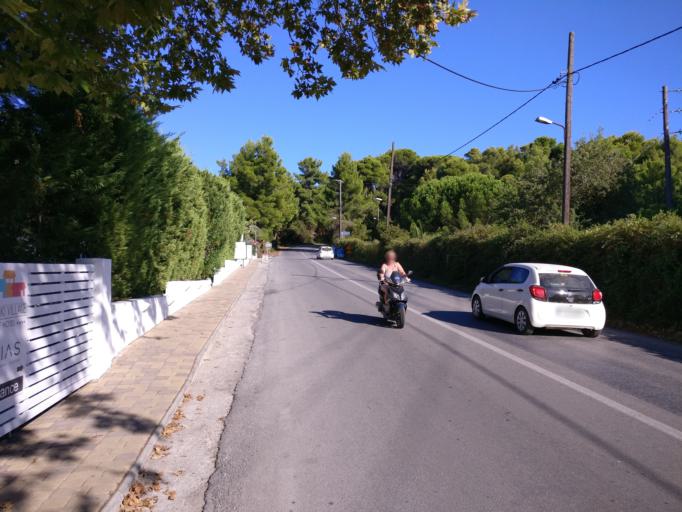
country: GR
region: Thessaly
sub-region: Nomos Magnisias
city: Skiathos
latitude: 39.1523
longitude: 23.4063
